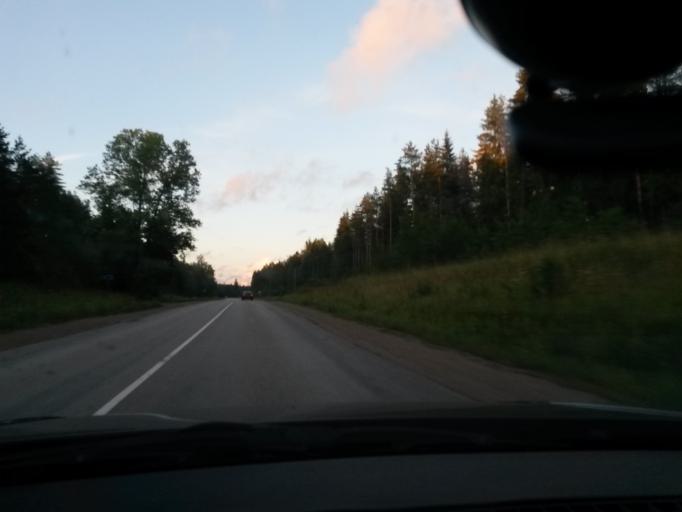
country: LV
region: Madonas Rajons
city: Madona
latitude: 56.8147
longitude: 26.1212
